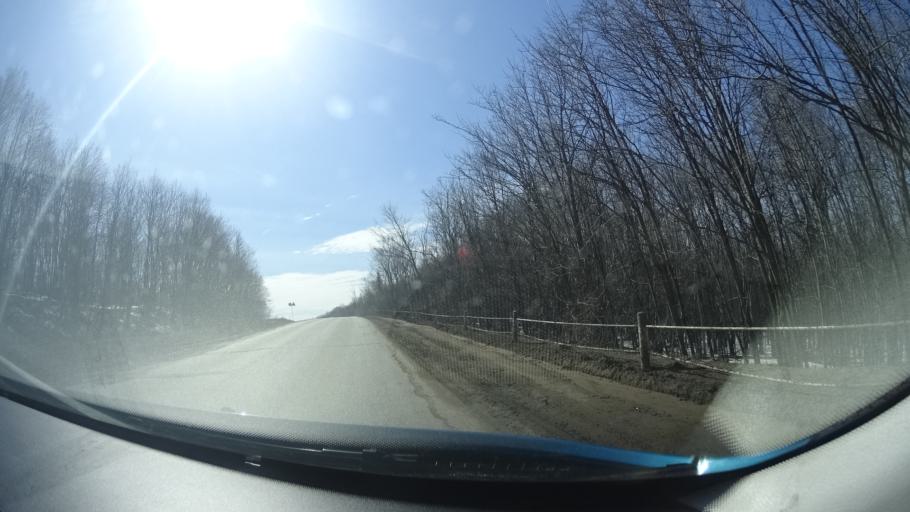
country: RU
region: Bashkortostan
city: Oktyabr'skiy
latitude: 54.4712
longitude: 53.5763
